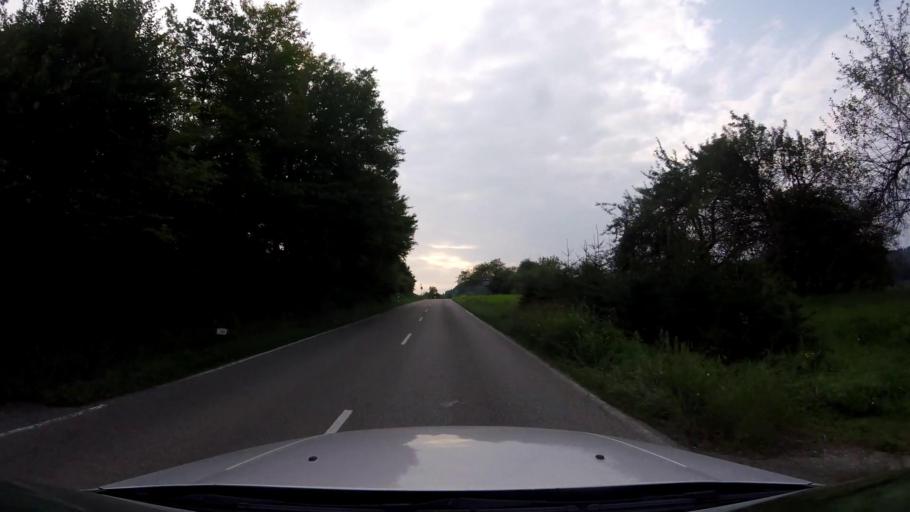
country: DE
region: Baden-Wuerttemberg
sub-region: Regierungsbezirk Stuttgart
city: Rudersberg
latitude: 48.8867
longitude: 9.5192
